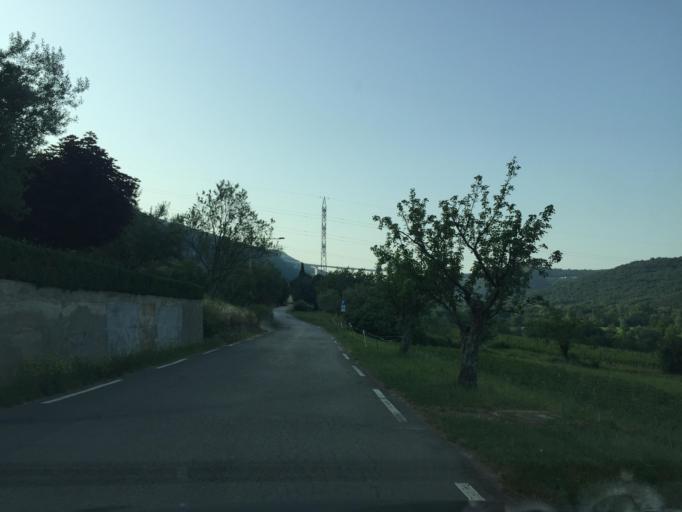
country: IT
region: Friuli Venezia Giulia
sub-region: Provincia di Trieste
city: Dolina
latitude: 45.5756
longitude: 13.8521
